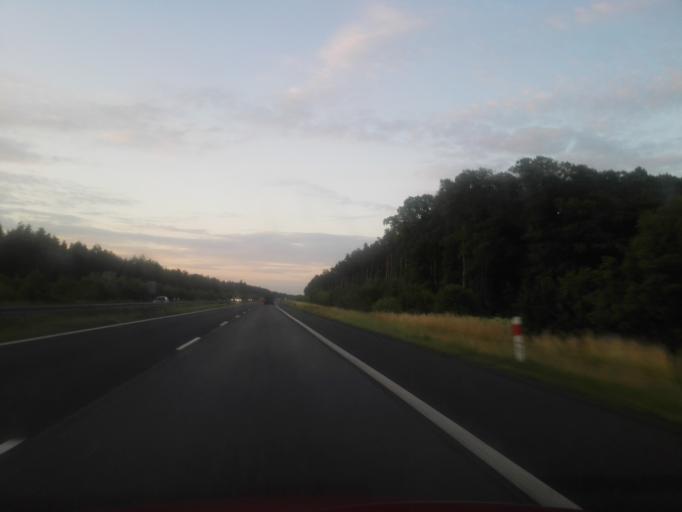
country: PL
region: Silesian Voivodeship
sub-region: Powiat czestochowski
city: Borowno
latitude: 50.9995
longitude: 19.2932
